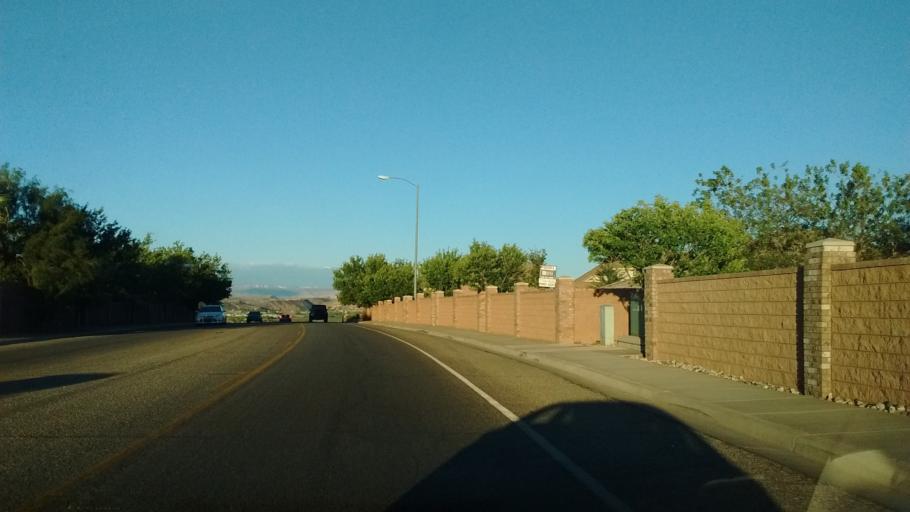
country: US
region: Utah
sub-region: Washington County
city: Saint George
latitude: 37.0934
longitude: -113.5466
